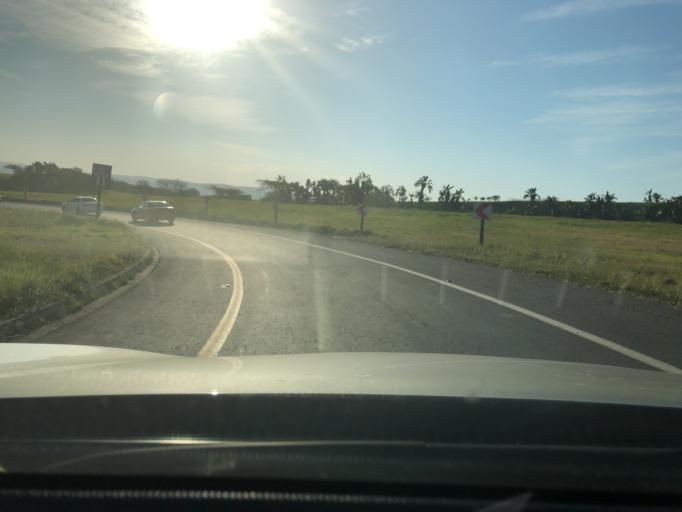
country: ZA
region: KwaZulu-Natal
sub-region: iLembe District Municipality
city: Stanger
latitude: -29.3463
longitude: 31.3249
